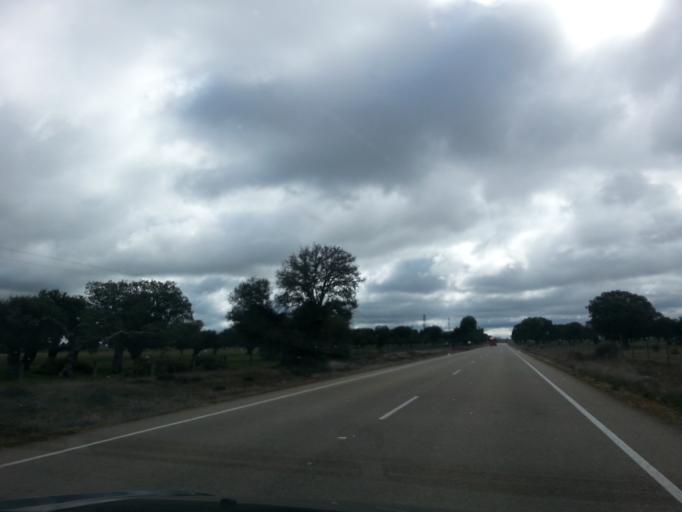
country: ES
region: Castille and Leon
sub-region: Provincia de Salamanca
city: Abusejo
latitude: 40.7268
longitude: -6.1576
